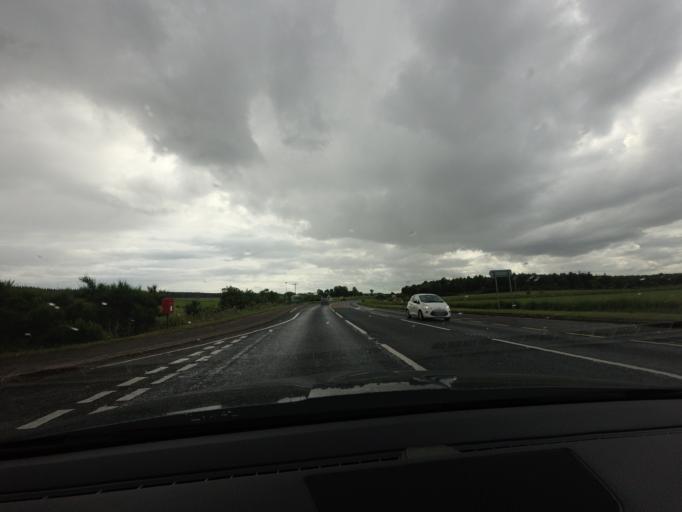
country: GB
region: Scotland
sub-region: Highland
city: Fortrose
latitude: 57.5231
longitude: -4.0628
